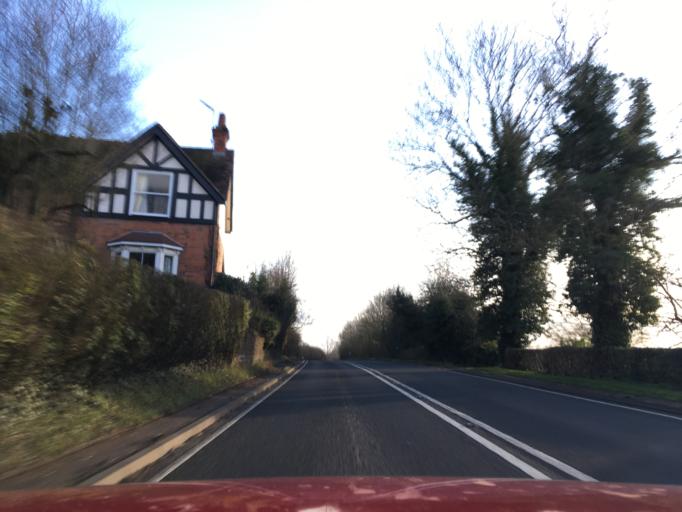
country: GB
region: England
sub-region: Warwickshire
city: Stratford-upon-Avon
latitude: 52.2310
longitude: -1.7409
